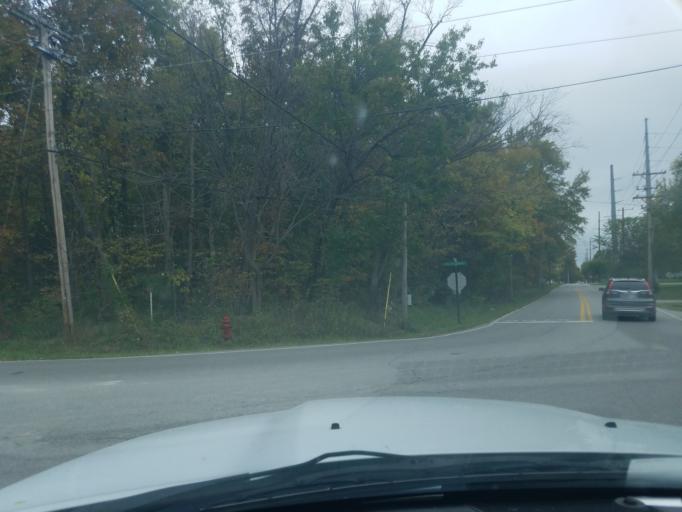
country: US
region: Indiana
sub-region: Clark County
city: Oak Park
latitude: 38.3487
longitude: -85.6999
